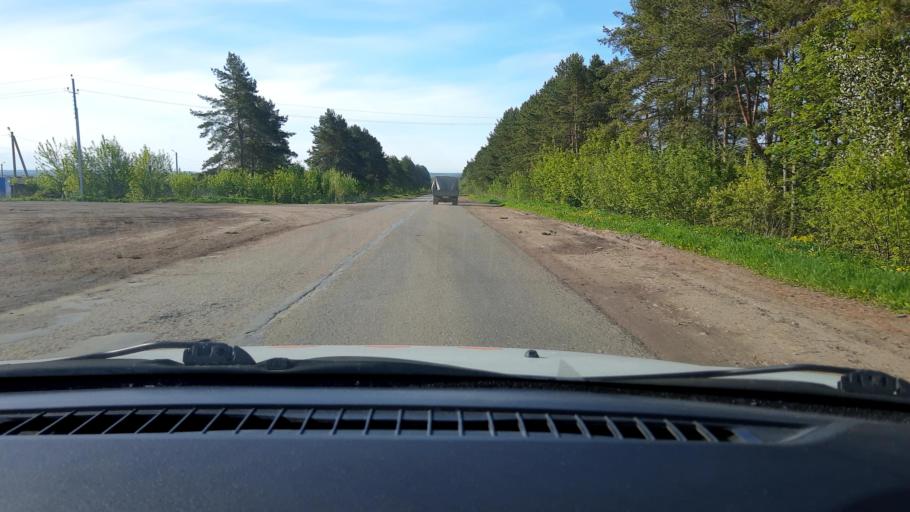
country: RU
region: Nizjnij Novgorod
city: Burevestnik
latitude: 56.1533
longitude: 43.7771
